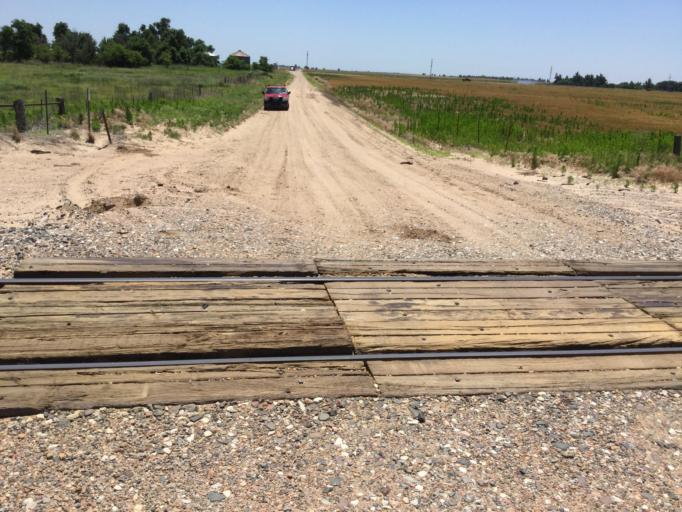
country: US
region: Kansas
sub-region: Edwards County
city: Kinsley
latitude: 37.9455
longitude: -99.1872
